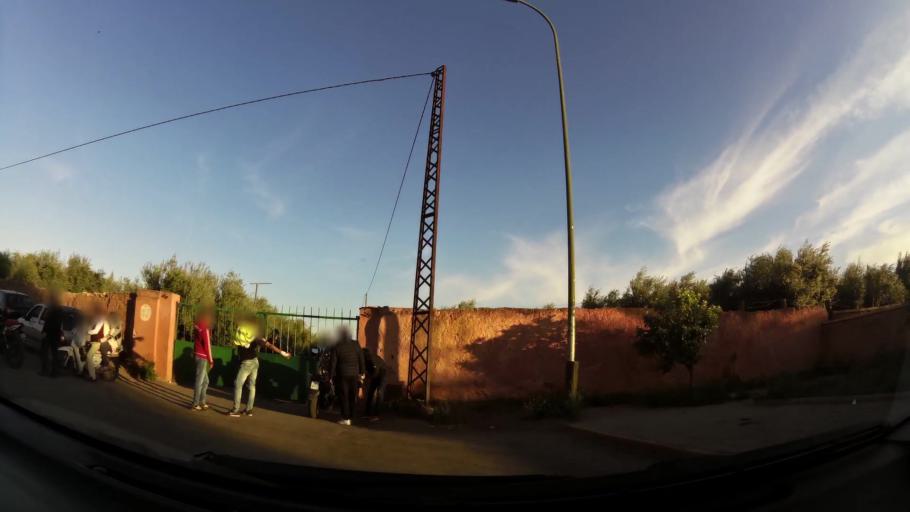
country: MA
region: Marrakech-Tensift-Al Haouz
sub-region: Marrakech
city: Marrakesh
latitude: 31.6189
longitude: -8.0259
